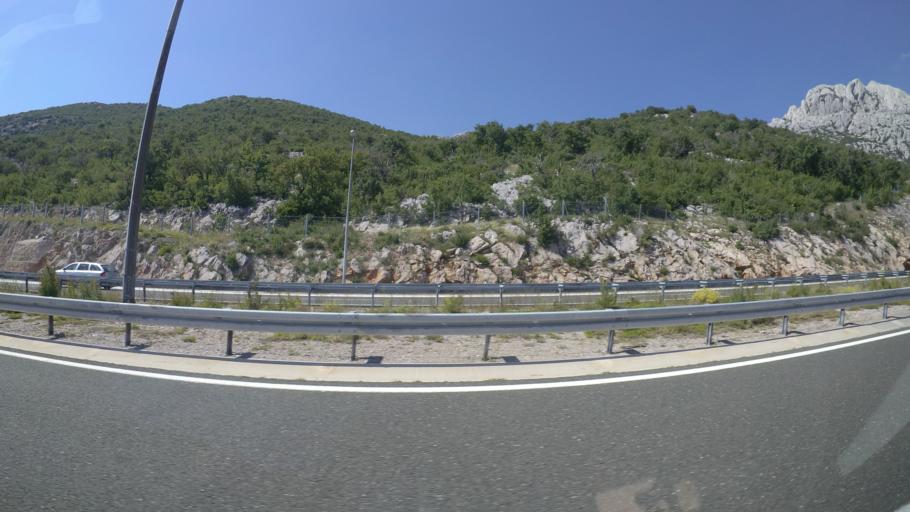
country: HR
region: Zadarska
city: Obrovac
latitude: 44.2515
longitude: 15.6432
